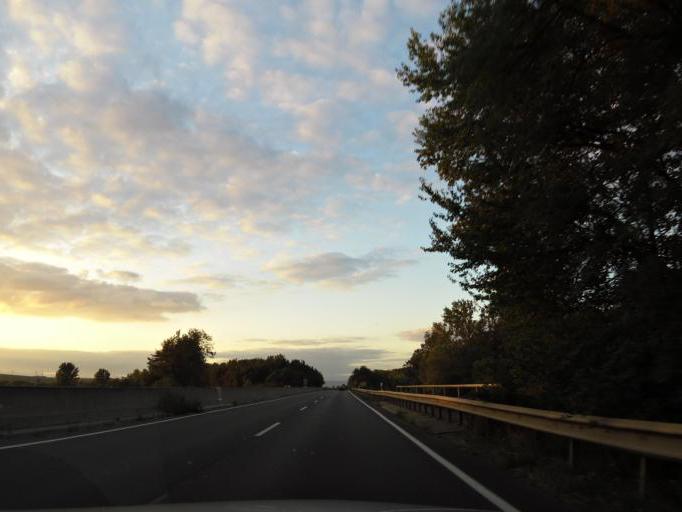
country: DE
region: Rheinland-Pfalz
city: Nackenheim
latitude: 49.9276
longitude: 8.3436
